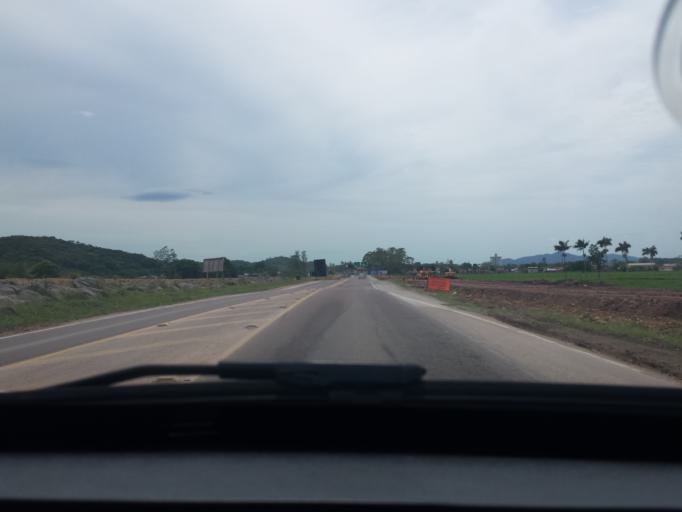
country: BR
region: Santa Catarina
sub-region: Gaspar
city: Gaspar
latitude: -26.9128
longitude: -48.9585
